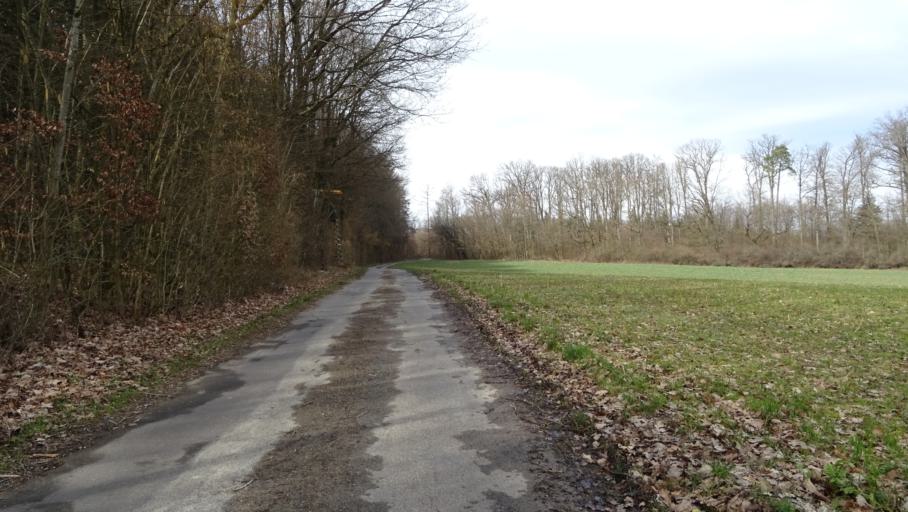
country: DE
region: Baden-Wuerttemberg
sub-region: Karlsruhe Region
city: Limbach
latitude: 49.4387
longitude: 9.2655
